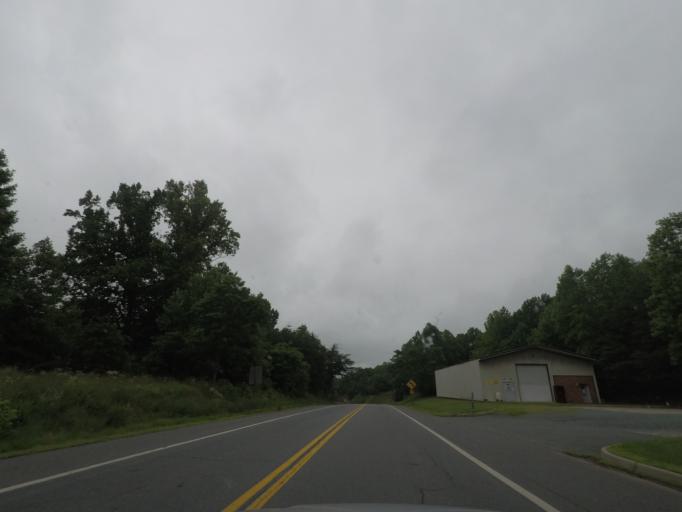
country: US
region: Virginia
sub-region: Fluvanna County
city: Weber City
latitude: 37.7063
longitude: -78.3048
